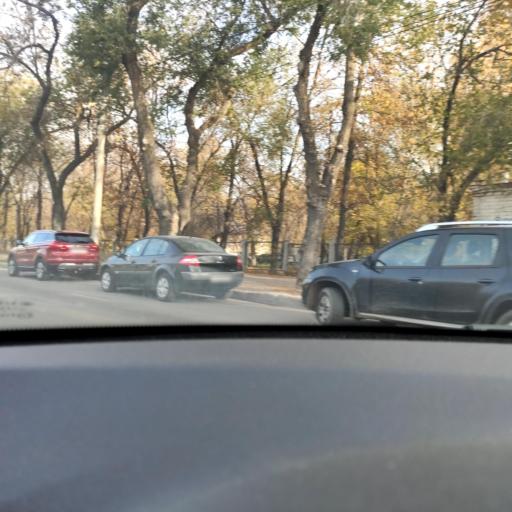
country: RU
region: Samara
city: Samara
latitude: 53.2196
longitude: 50.2400
